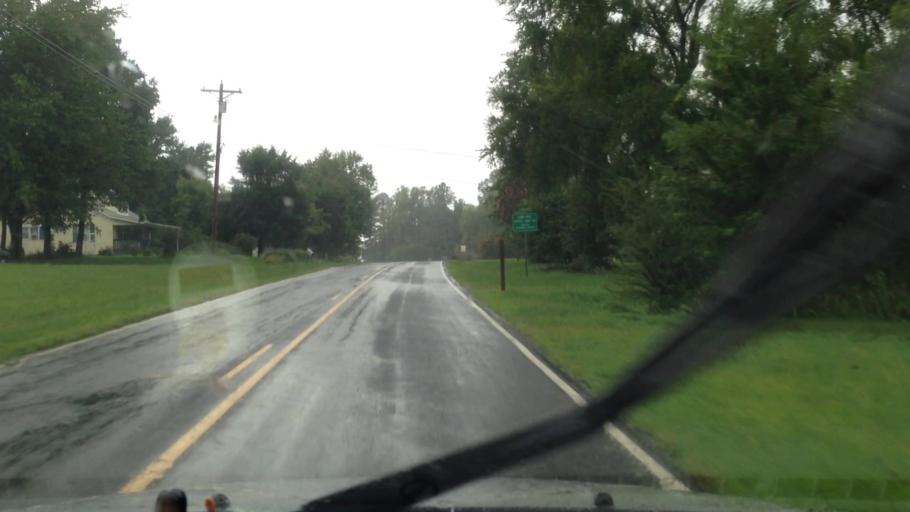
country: US
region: North Carolina
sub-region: Guilford County
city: Stokesdale
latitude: 36.2165
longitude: -80.0295
